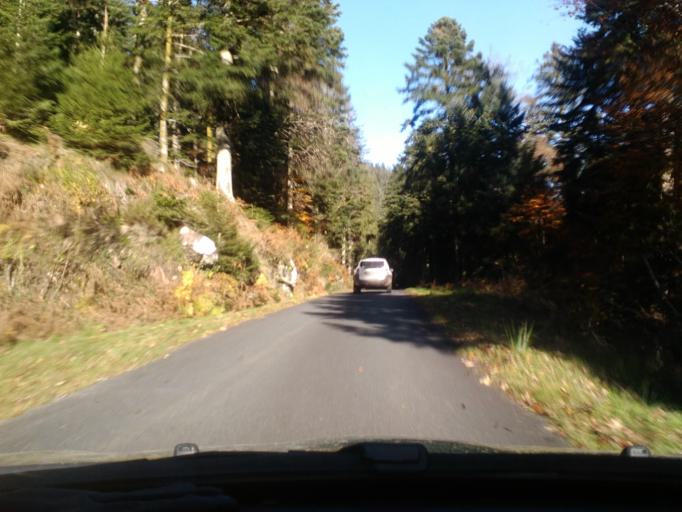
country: FR
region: Lorraine
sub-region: Departement des Vosges
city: Senones
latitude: 48.4594
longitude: 7.0606
